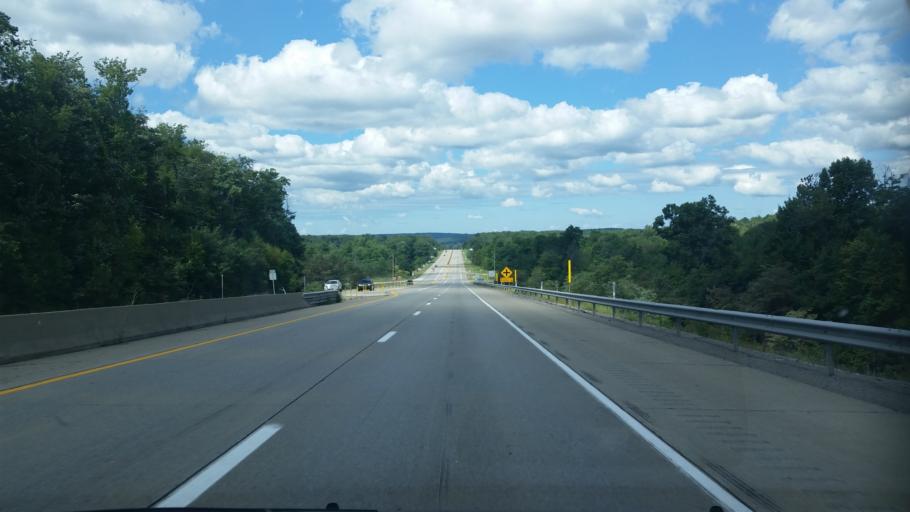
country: US
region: Pennsylvania
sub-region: Cambria County
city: Vinco
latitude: 40.4436
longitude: -78.9680
